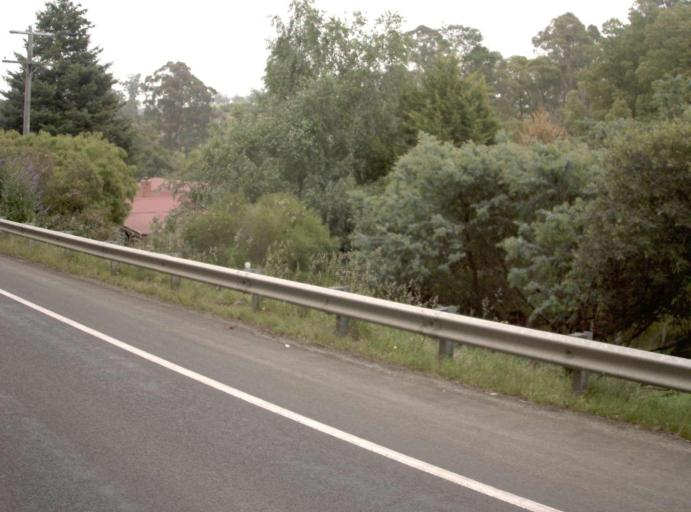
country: AU
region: Victoria
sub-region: Latrobe
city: Moe
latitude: -38.3821
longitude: 146.1748
